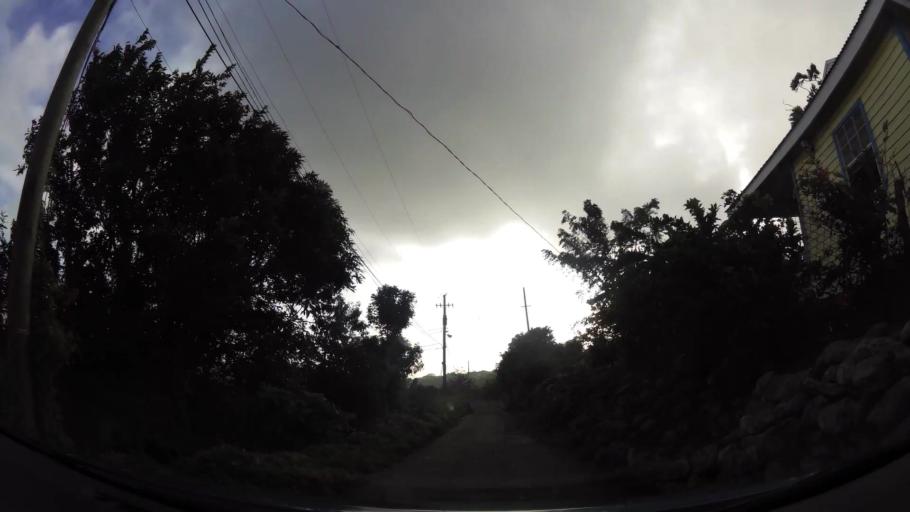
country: KN
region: Saint George Gingerland
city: Market Shop
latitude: 17.1389
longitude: -62.5756
